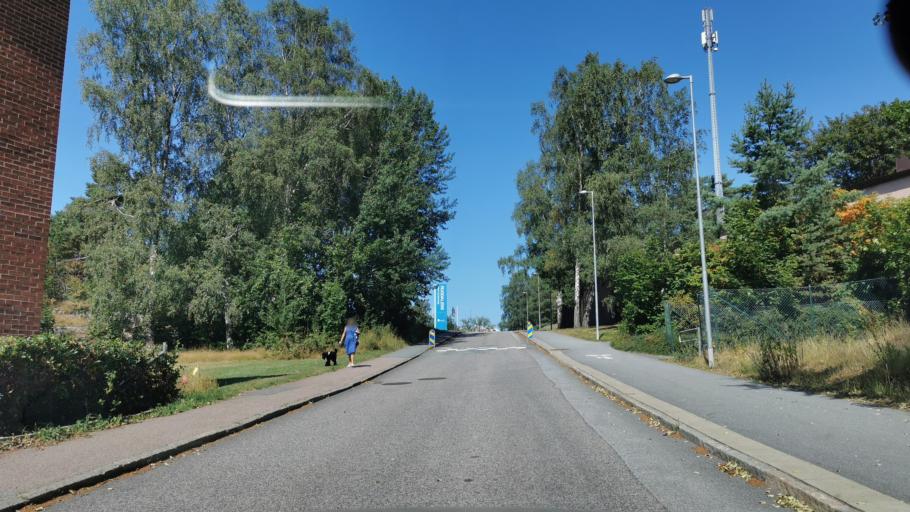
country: SE
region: Vaestra Goetaland
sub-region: Goteborg
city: Majorna
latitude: 57.6619
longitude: 11.9129
